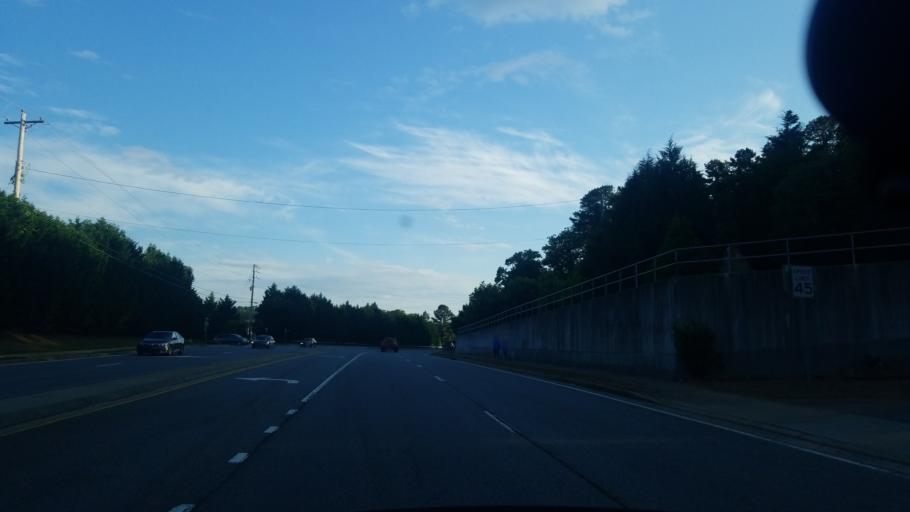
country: US
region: Georgia
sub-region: Fulton County
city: Johns Creek
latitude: 34.1009
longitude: -84.1591
